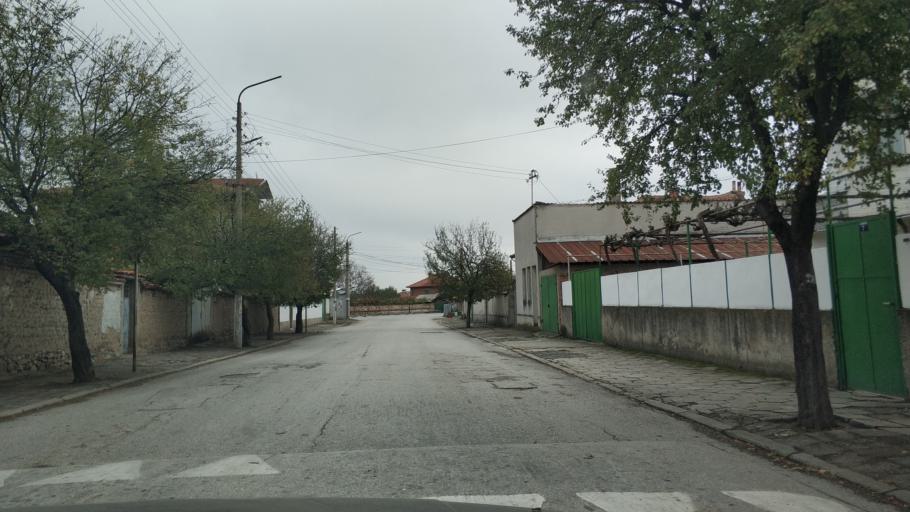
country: BG
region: Plovdiv
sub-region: Obshtina Kaloyanovo
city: Kaloyanovo
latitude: 42.3702
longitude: 24.7219
